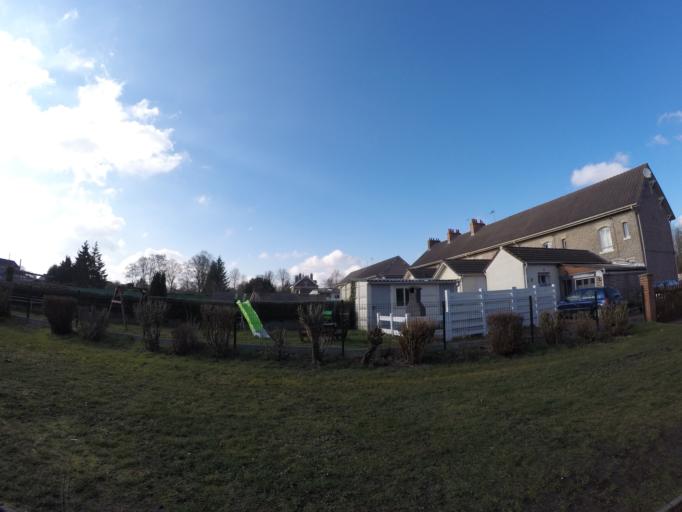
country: FR
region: Nord-Pas-de-Calais
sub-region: Departement du Pas-de-Calais
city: Bully-les-Mines
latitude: 50.4568
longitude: 2.7311
